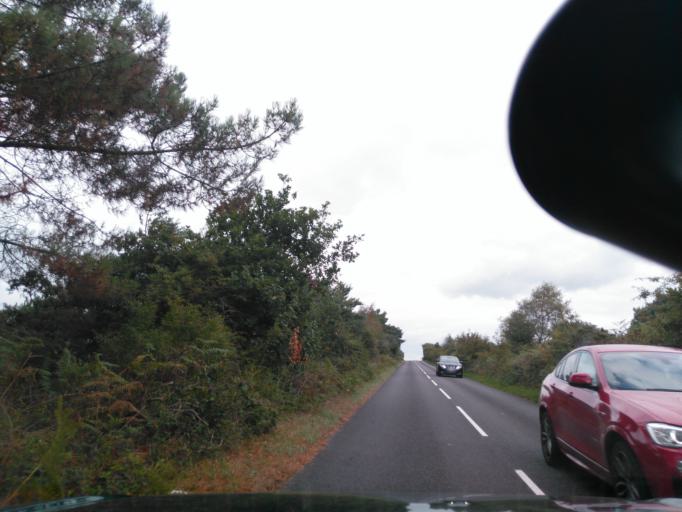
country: GB
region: England
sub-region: Dorset
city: Wareham
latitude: 50.7096
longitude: -2.1082
